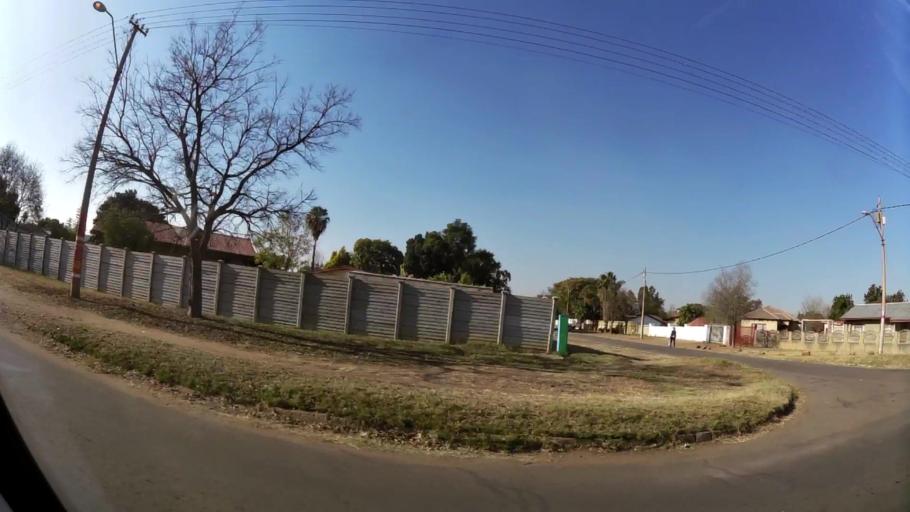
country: ZA
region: North-West
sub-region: Bojanala Platinum District Municipality
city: Rustenburg
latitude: -25.6589
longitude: 27.2593
